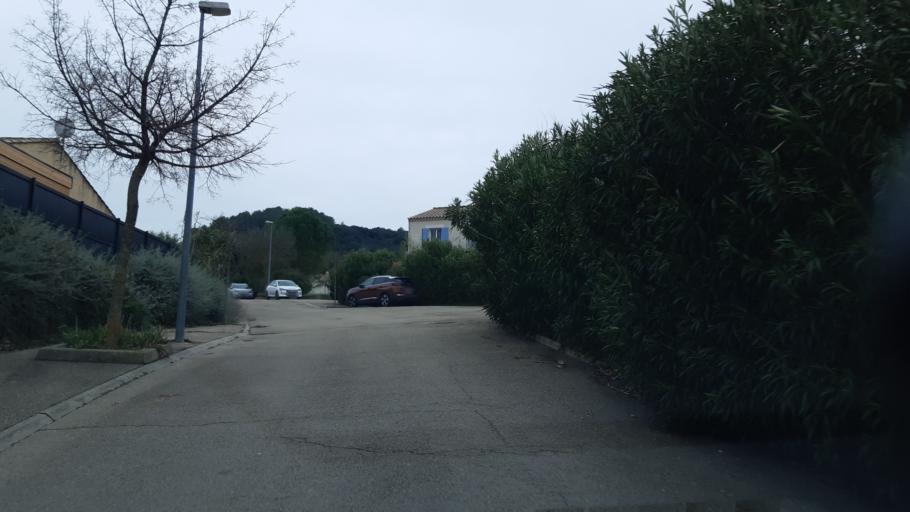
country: FR
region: Languedoc-Roussillon
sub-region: Departement du Gard
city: Comps
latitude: 43.8454
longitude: 4.6025
